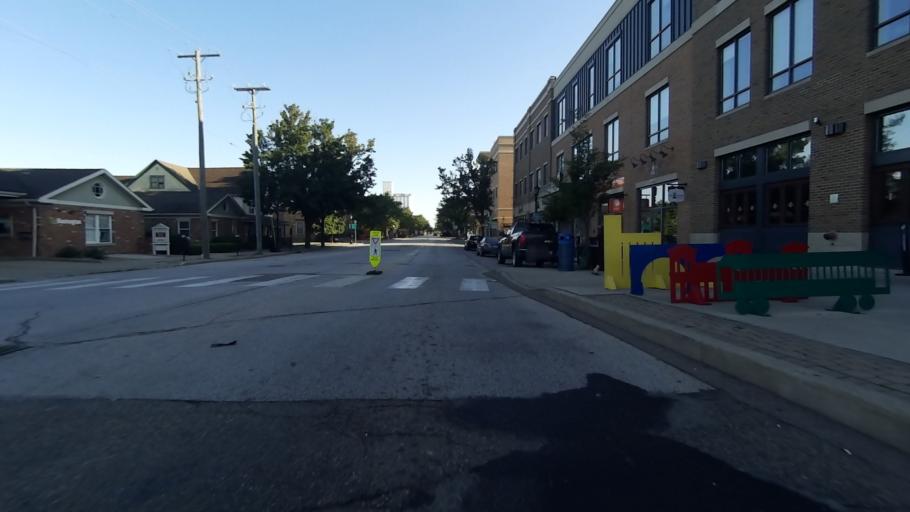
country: US
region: Ohio
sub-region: Portage County
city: Kent
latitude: 41.1517
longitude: -81.3581
